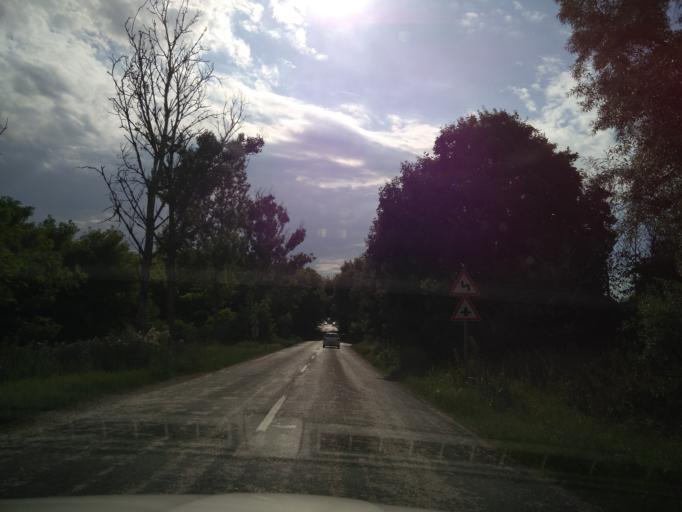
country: HU
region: Pest
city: Zsambek
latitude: 47.4965
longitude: 18.7205
